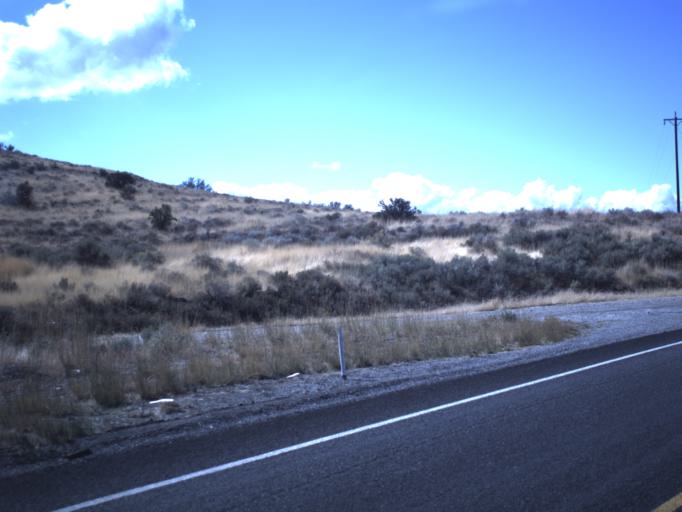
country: US
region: Utah
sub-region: Utah County
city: Santaquin
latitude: 40.0044
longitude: -111.8065
